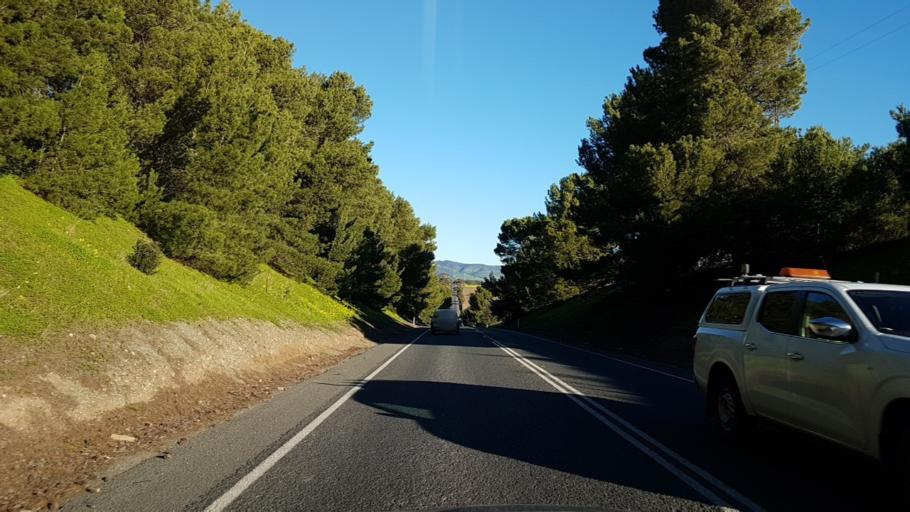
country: AU
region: South Australia
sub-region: Onkaparinga
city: Aldinga
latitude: -35.2393
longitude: 138.4938
